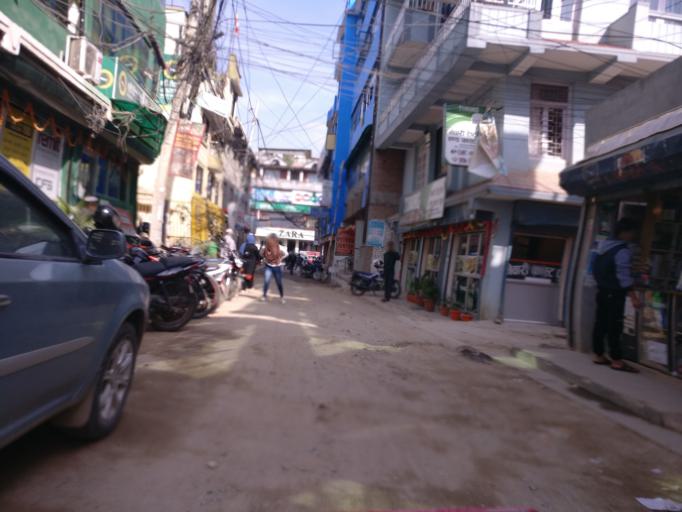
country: NP
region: Central Region
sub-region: Bagmati Zone
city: Patan
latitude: 27.6705
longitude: 85.3196
